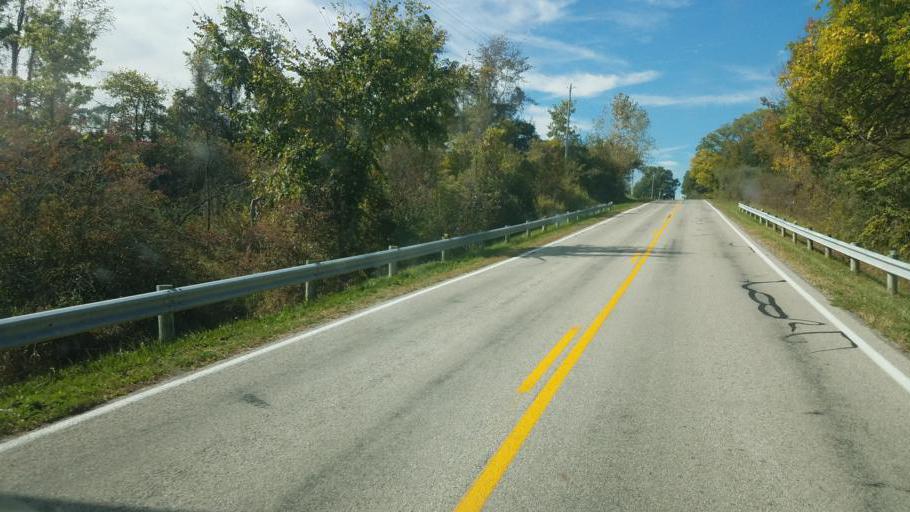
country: US
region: Ohio
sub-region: Erie County
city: Huron
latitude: 41.3650
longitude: -82.5071
